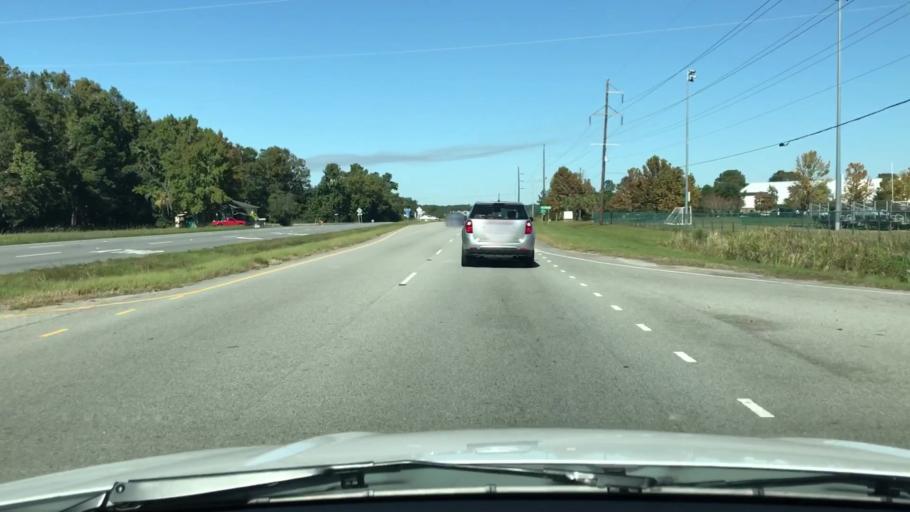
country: US
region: South Carolina
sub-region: Beaufort County
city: Laurel Bay
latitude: 32.5320
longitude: -80.7471
